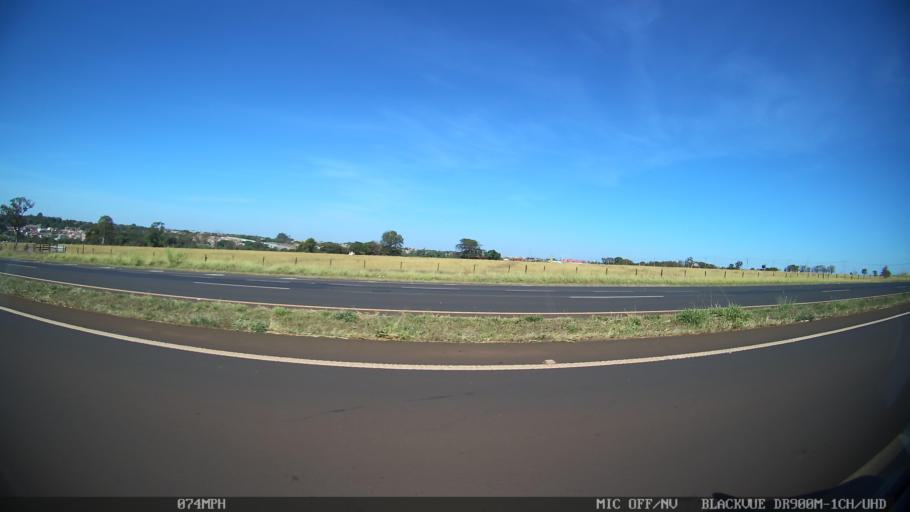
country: BR
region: Sao Paulo
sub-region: Barretos
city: Barretos
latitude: -20.5264
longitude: -48.5889
